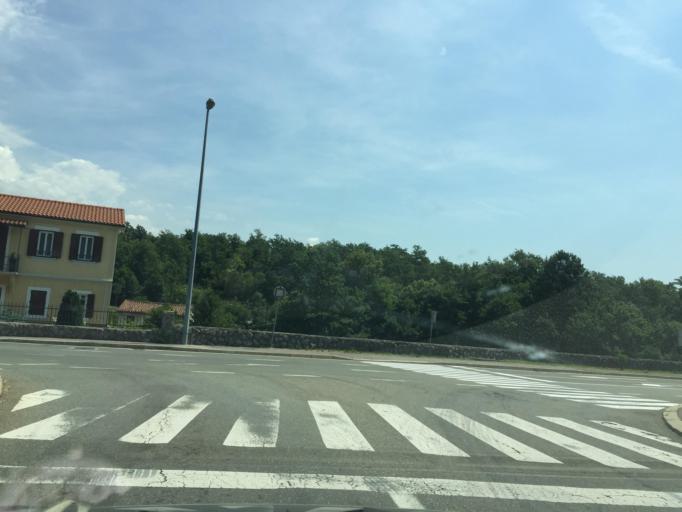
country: HR
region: Primorsko-Goranska
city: Matulji
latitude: 45.3982
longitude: 14.3082
